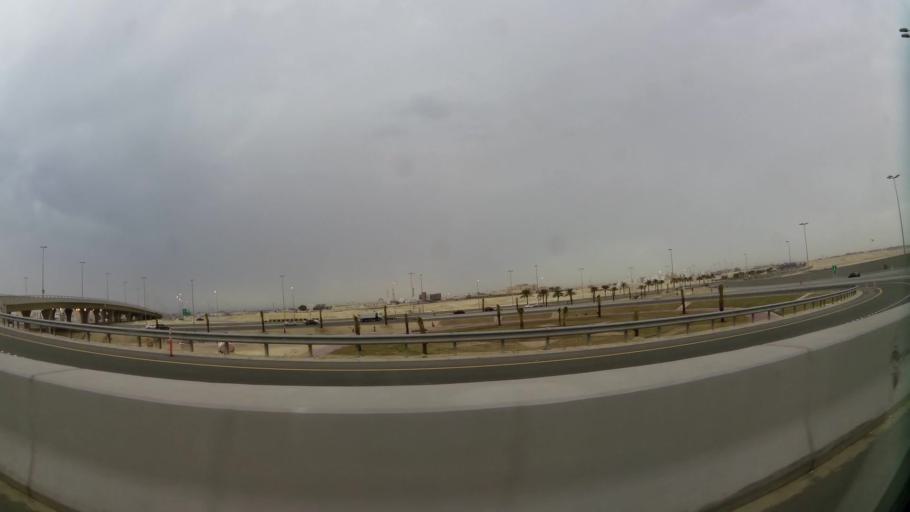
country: BH
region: Central Governorate
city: Dar Kulayb
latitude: 26.0822
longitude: 50.5167
